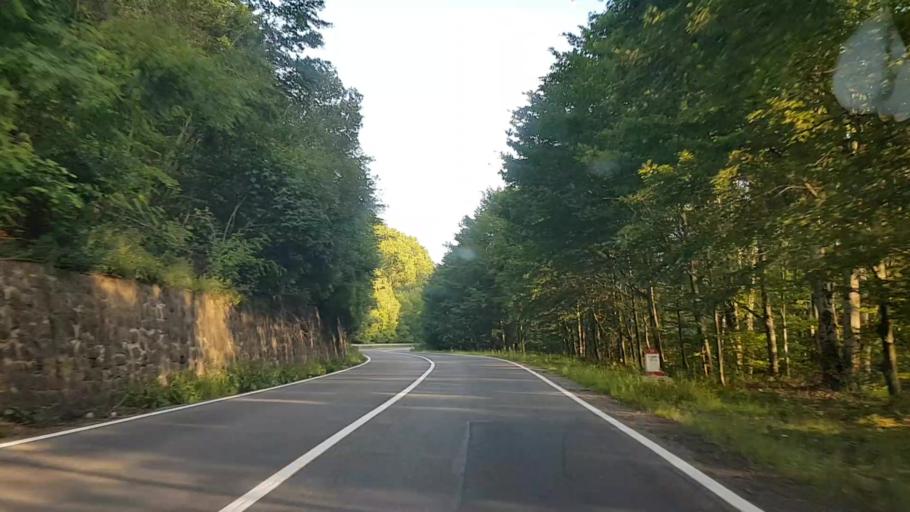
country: RO
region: Harghita
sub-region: Comuna Corund
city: Corund
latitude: 46.4460
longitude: 25.2282
